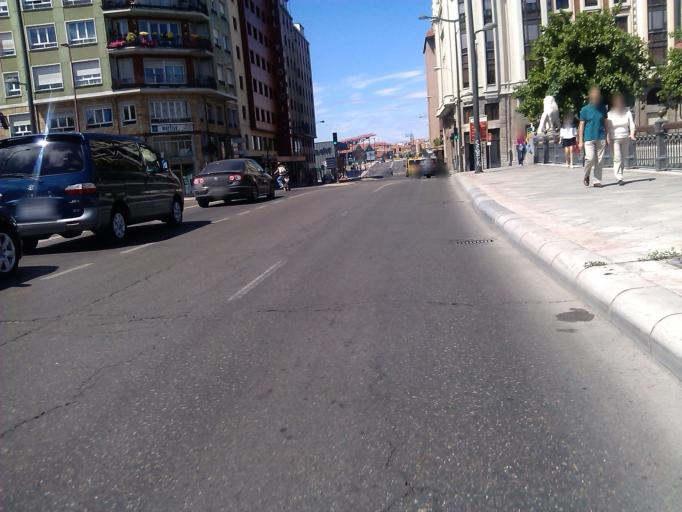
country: ES
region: Castille and Leon
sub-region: Provincia de Leon
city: Leon
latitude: 42.5961
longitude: -5.5795
